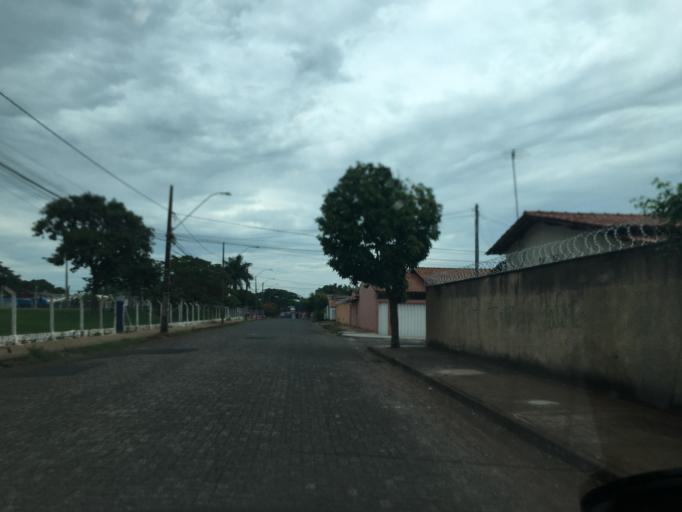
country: BR
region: Minas Gerais
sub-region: Uberlandia
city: Uberlandia
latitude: -18.9318
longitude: -48.3181
